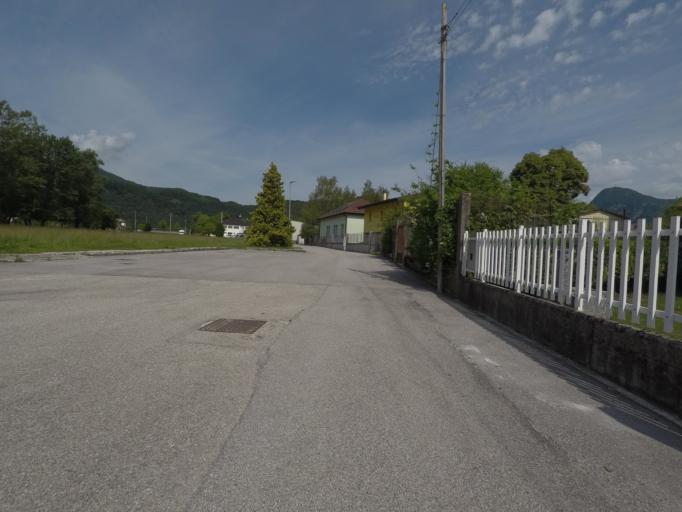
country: IT
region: Friuli Venezia Giulia
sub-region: Provincia di Udine
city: Cavazzo Carnico
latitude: 46.3665
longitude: 13.0436
